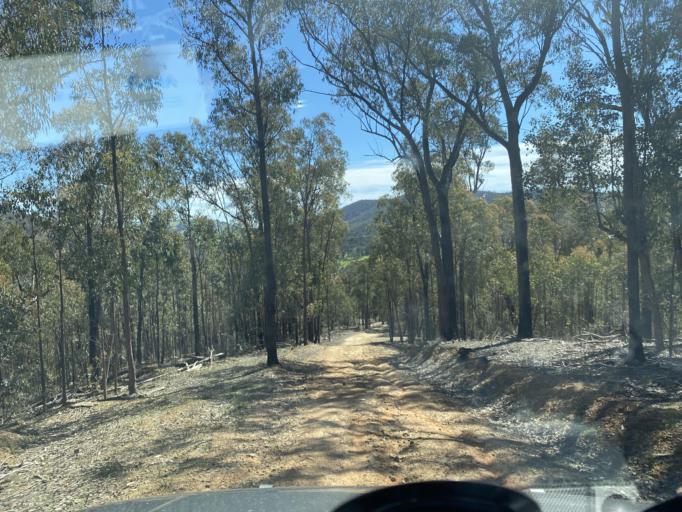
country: AU
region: Victoria
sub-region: Benalla
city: Benalla
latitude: -36.7176
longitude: 146.1809
